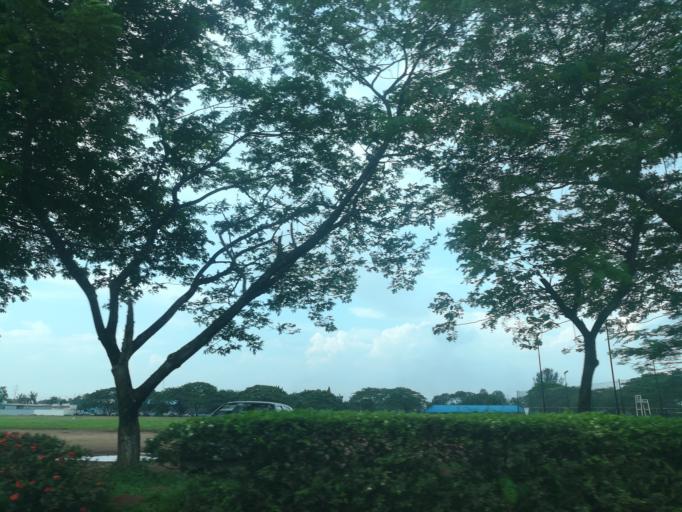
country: NG
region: Lagos
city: Ikorodu
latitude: 6.6458
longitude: 3.5195
